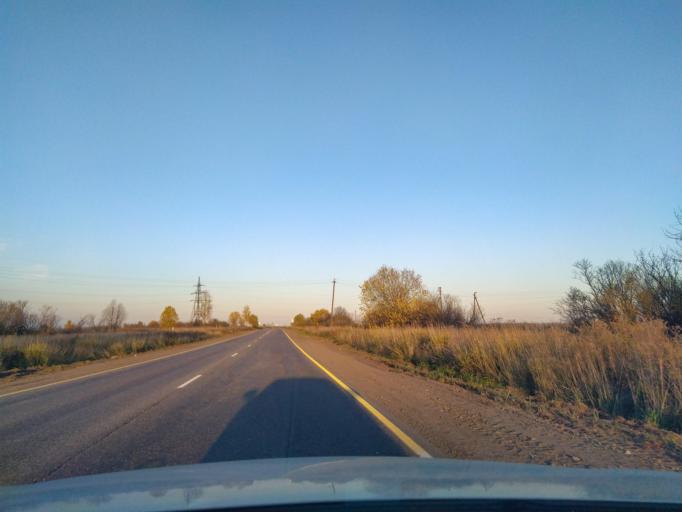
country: RU
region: Leningrad
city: Kobrinskoye
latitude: 59.4793
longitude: 30.1441
